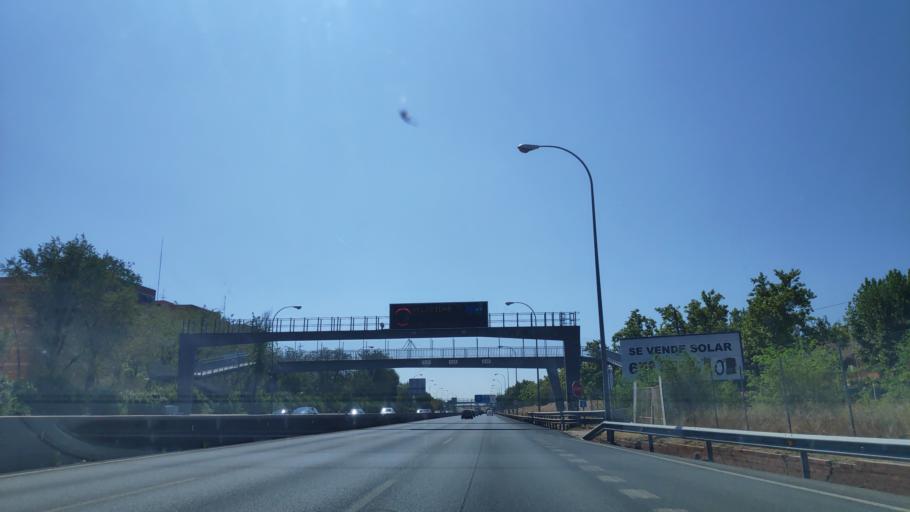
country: ES
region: Madrid
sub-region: Provincia de Madrid
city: Getafe
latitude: 40.3027
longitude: -3.7390
